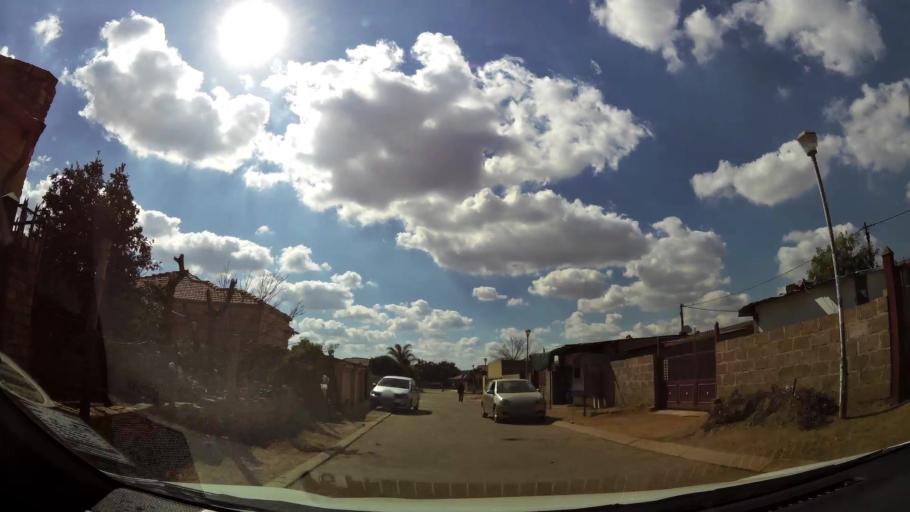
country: ZA
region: Gauteng
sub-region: City of Tshwane Metropolitan Municipality
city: Cullinan
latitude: -25.7085
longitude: 28.4091
